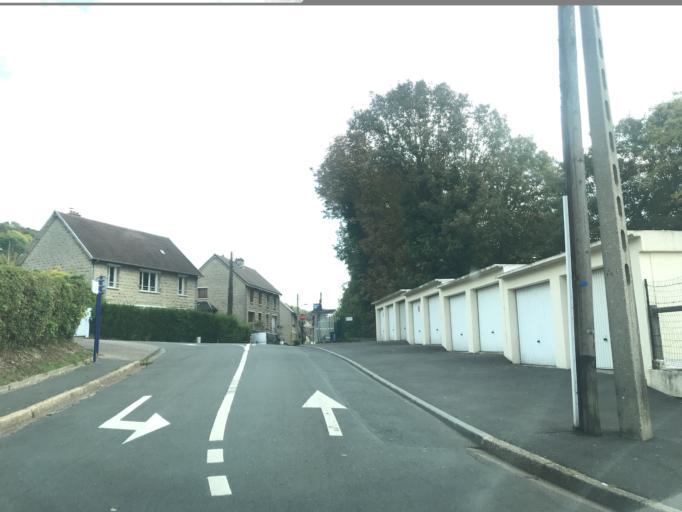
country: FR
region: Haute-Normandie
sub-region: Departement de la Seine-Maritime
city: Deville-les-Rouen
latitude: 49.4610
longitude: 1.0570
